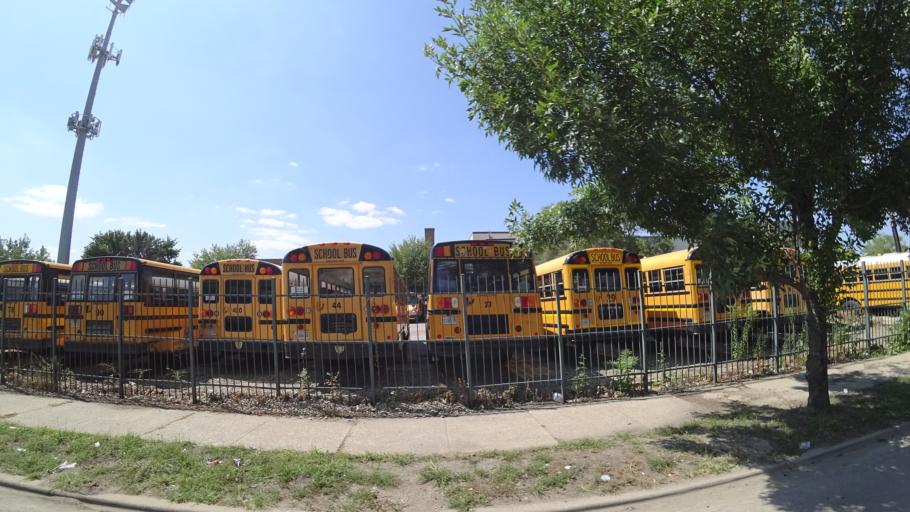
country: US
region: Illinois
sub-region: Cook County
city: Cicero
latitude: 41.8554
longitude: -87.7347
